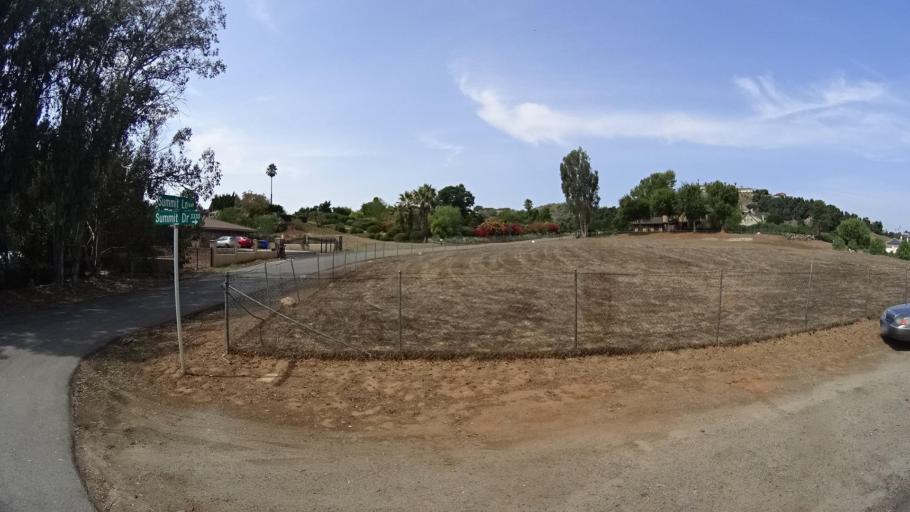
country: US
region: California
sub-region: San Diego County
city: Escondido
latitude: 33.0956
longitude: -117.0315
